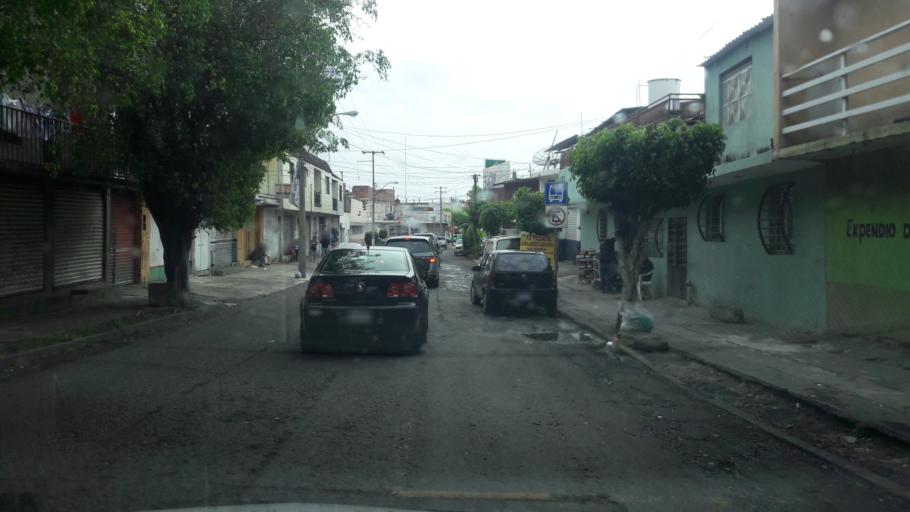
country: MX
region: Guanajuato
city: Leon
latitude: 21.1176
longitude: -101.6898
